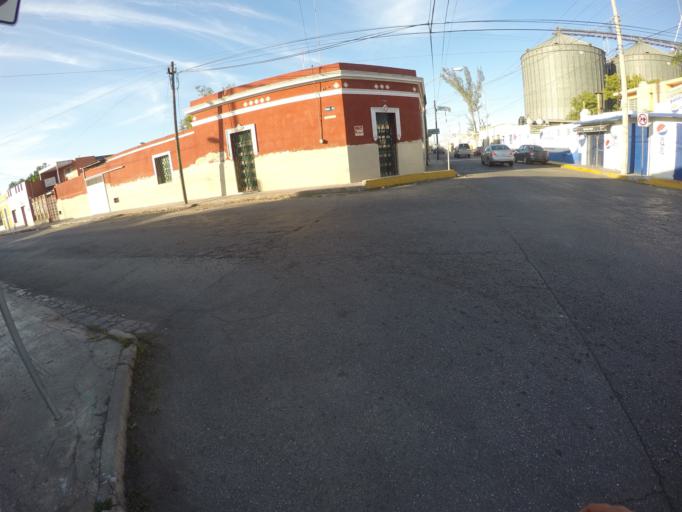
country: MX
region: Yucatan
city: Merida
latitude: 20.9783
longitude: -89.6154
